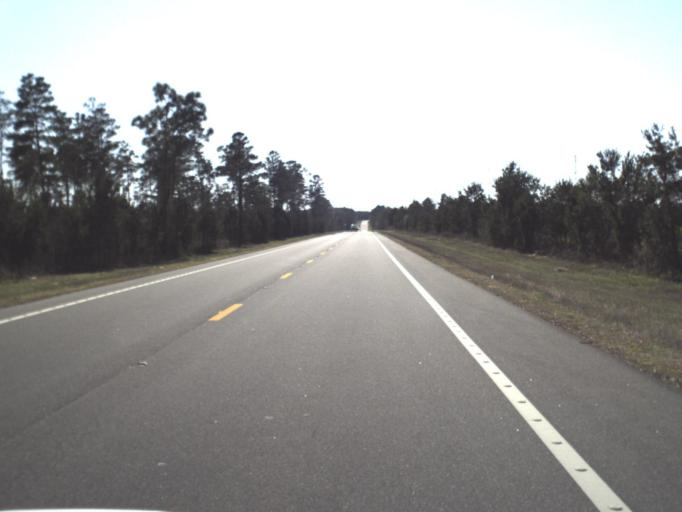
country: US
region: Florida
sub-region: Bay County
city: Youngstown
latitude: 30.4306
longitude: -85.2866
